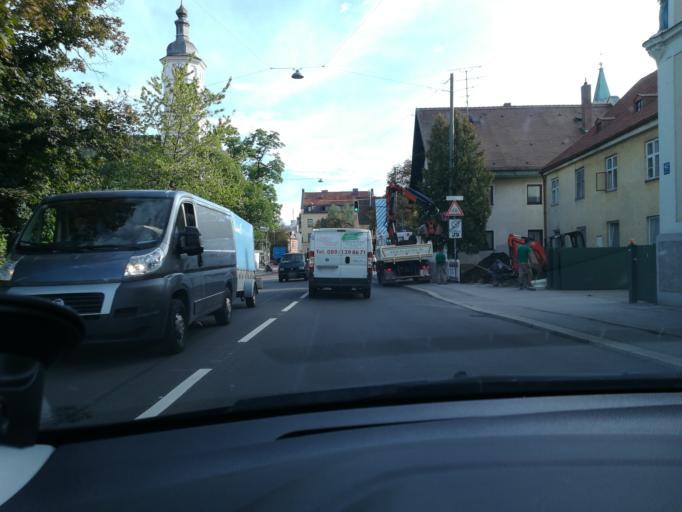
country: DE
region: Bavaria
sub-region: Upper Bavaria
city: Munich
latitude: 48.1221
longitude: 11.5411
